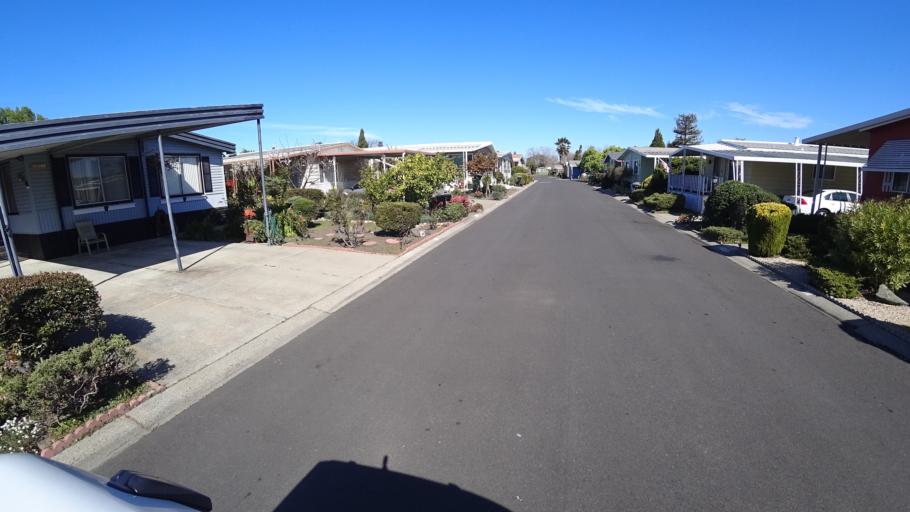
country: US
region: California
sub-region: Alameda County
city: Hayward
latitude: 37.6216
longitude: -122.0985
